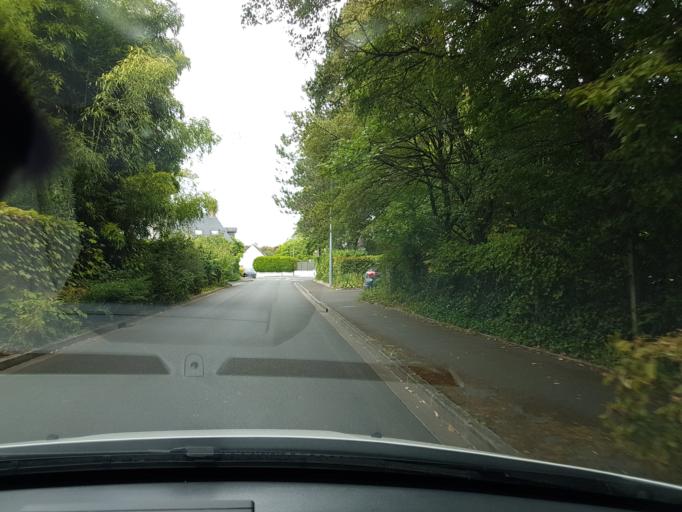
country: FR
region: Centre
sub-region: Departement d'Indre-et-Loire
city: Saint-Avertin
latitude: 47.3547
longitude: 0.7483
